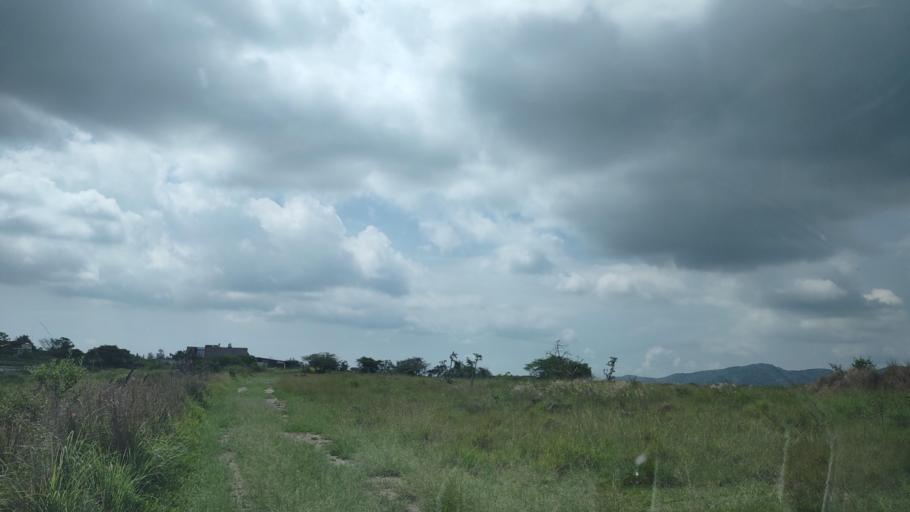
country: MX
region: Veracruz
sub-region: Emiliano Zapata
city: Dos Rios
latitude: 19.4616
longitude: -96.7961
